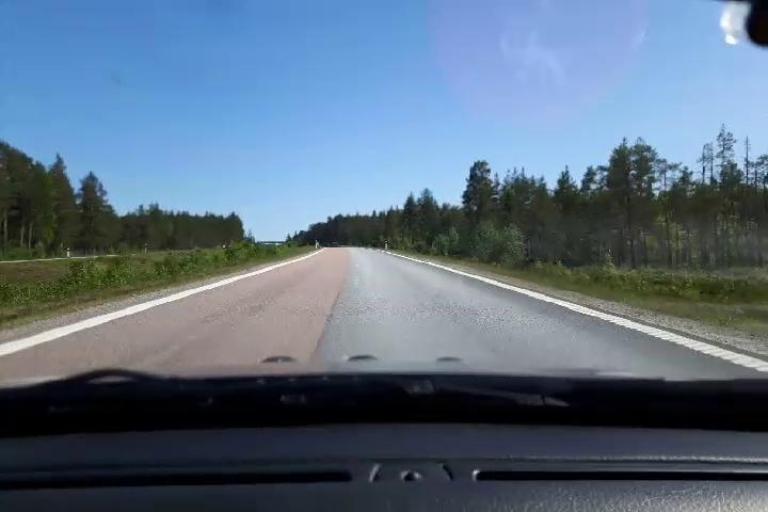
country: SE
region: Gaevleborg
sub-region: Soderhamns Kommun
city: Soderhamn
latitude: 61.3764
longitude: 16.9968
